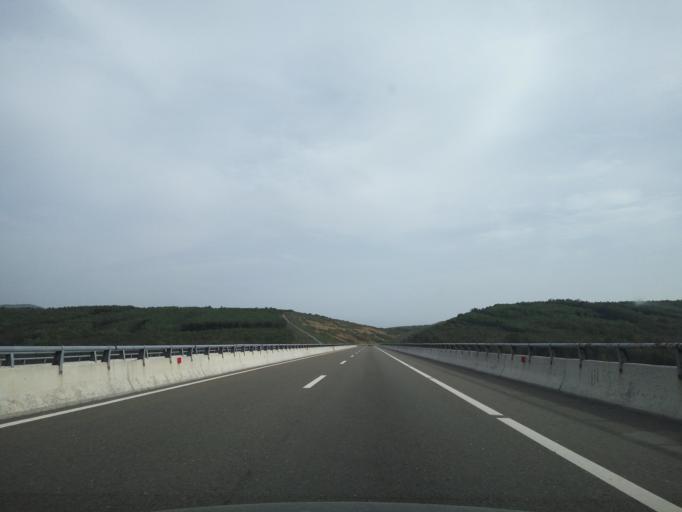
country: XK
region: Prizren
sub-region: Komuna e Malisheves
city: Llazice
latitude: 42.5216
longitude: 20.8030
